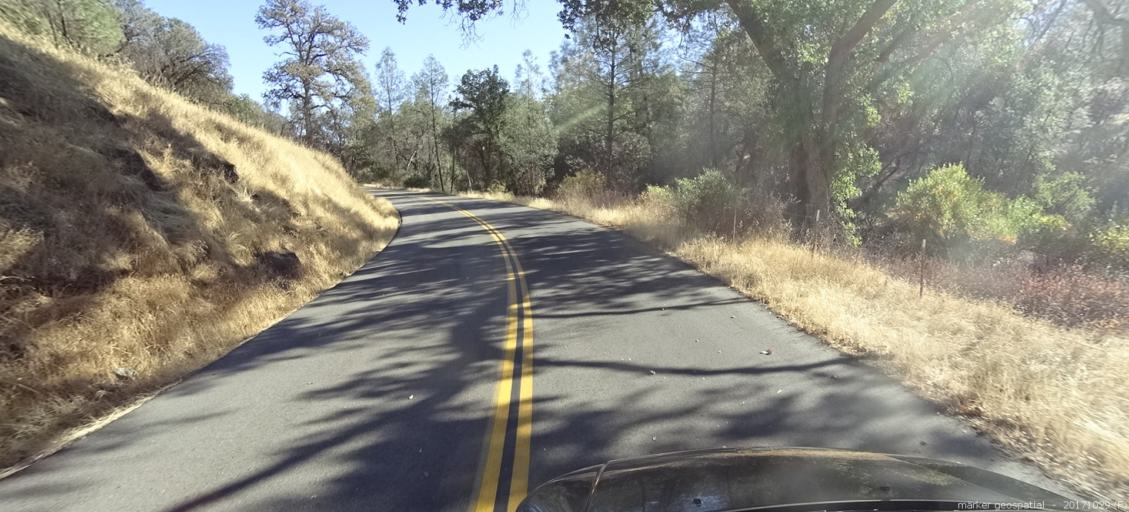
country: US
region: California
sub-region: Shasta County
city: Shasta
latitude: 40.4269
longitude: -122.7238
